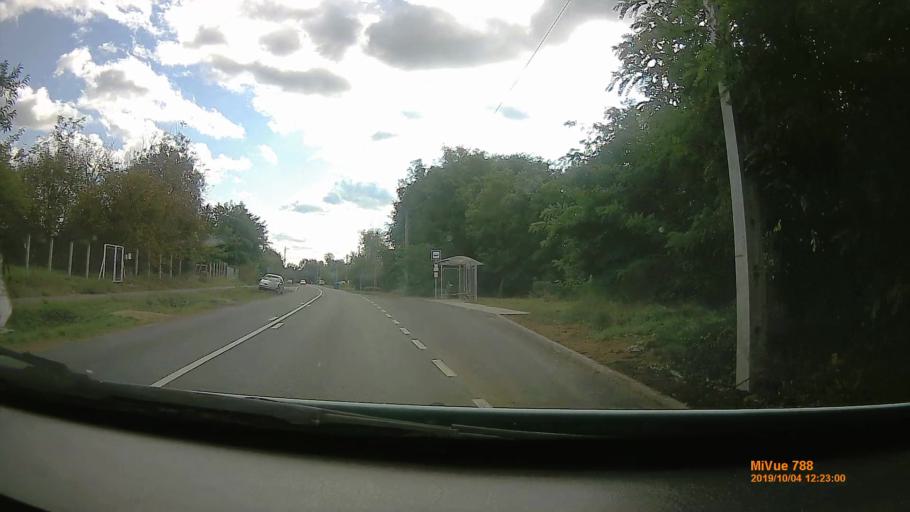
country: HU
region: Szabolcs-Szatmar-Bereg
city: Kotaj
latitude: 48.0087
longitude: 21.6945
